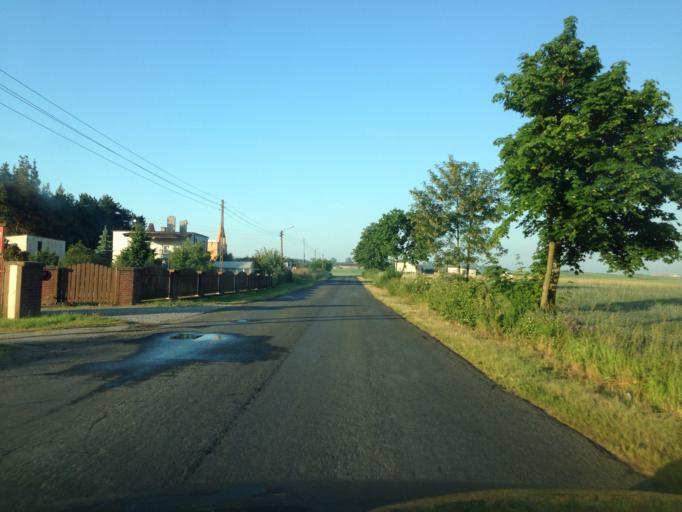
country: PL
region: Pomeranian Voivodeship
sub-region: Powiat tczewski
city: Gniew
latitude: 53.8108
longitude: 18.8167
